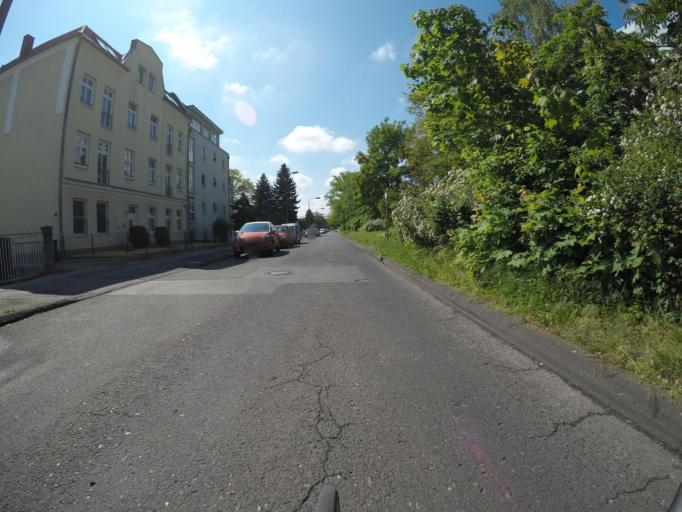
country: DE
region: Berlin
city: Biesdorf
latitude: 52.5248
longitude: 13.5482
